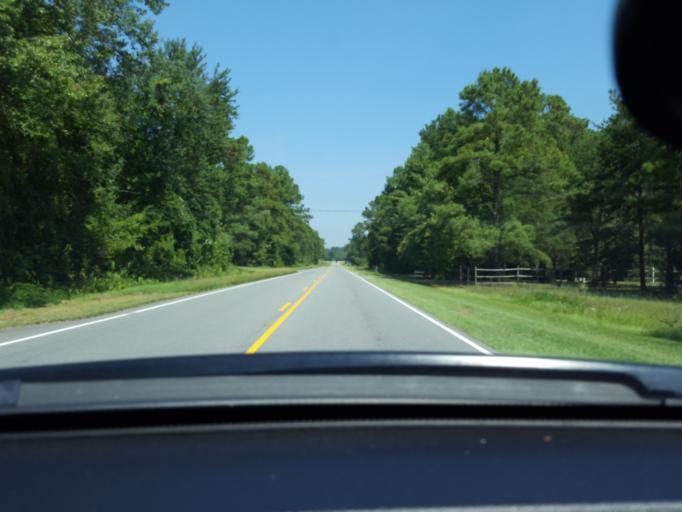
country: US
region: North Carolina
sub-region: Bladen County
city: Elizabethtown
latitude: 34.6715
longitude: -78.4901
